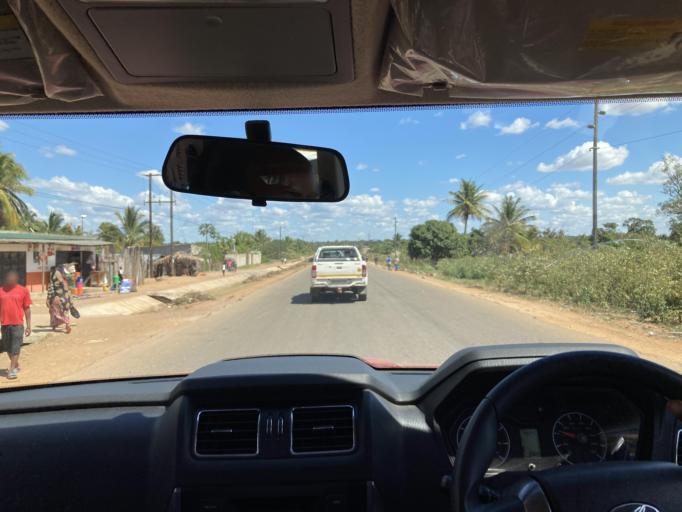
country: MZ
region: Cabo Delgado
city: Montepuez
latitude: -13.1342
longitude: 38.9912
